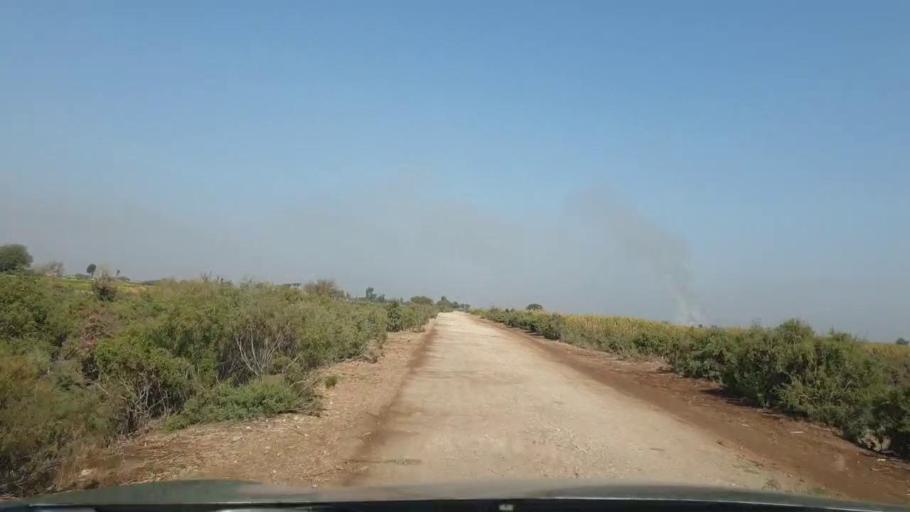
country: PK
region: Sindh
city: Mirpur Khas
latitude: 25.6400
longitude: 68.8970
